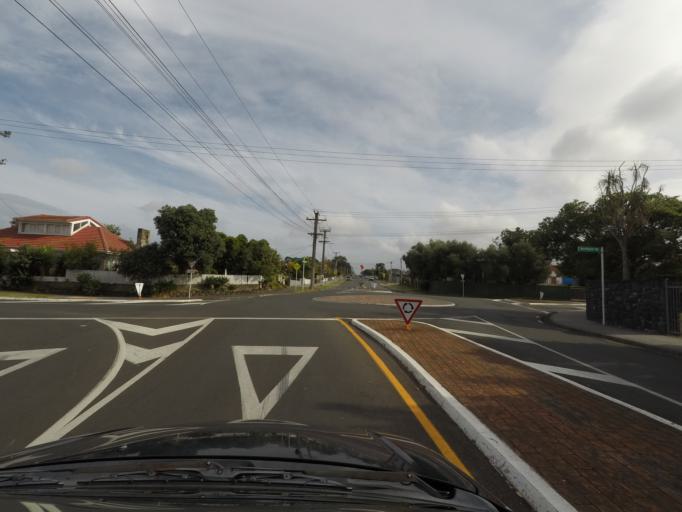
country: NZ
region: Auckland
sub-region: Auckland
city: Waitakere
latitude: -36.9004
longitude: 174.6665
